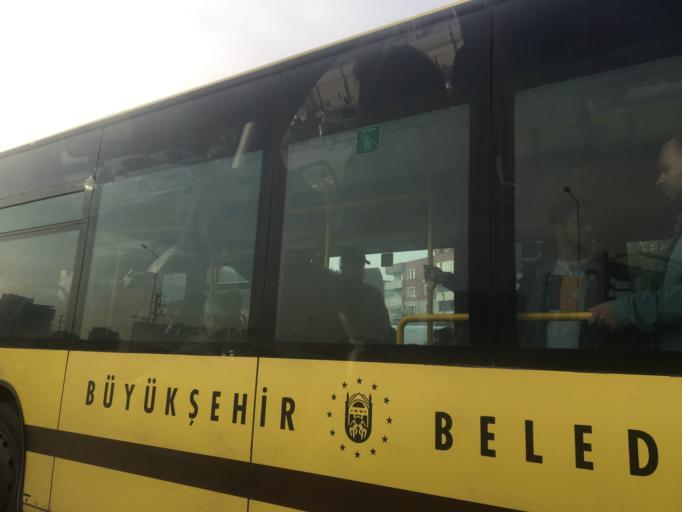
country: TR
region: Bursa
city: Yildirim
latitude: 40.2125
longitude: 28.9970
